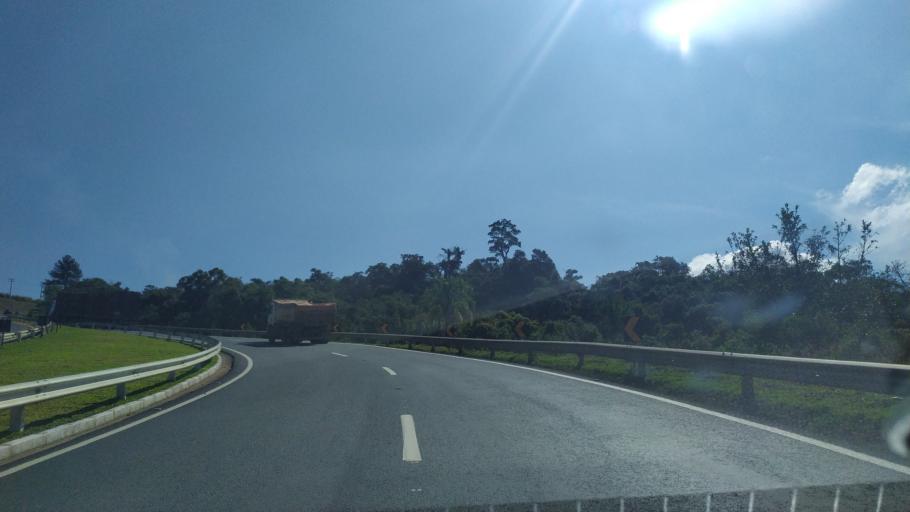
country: BR
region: Parana
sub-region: Telemaco Borba
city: Telemaco Borba
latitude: -24.2616
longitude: -50.7233
